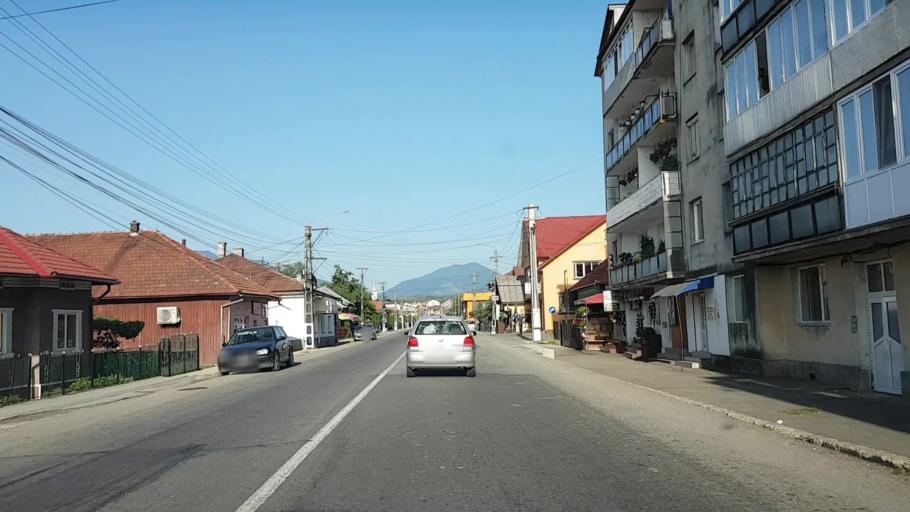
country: RO
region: Bistrita-Nasaud
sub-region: Comuna Prundu Bargaului
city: Susenii Bargaului
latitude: 47.2202
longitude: 24.7295
